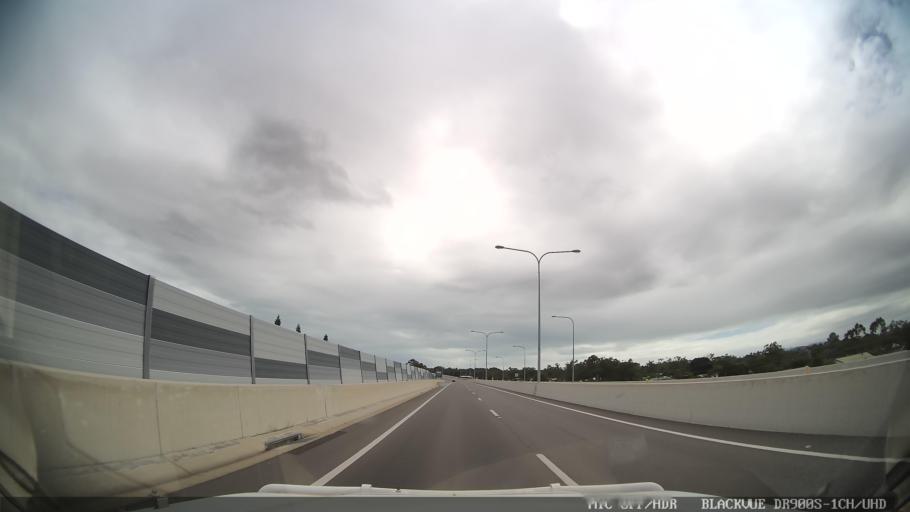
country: AU
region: Queensland
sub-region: Townsville
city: Bohle Plains
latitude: -19.2483
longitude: 146.6641
